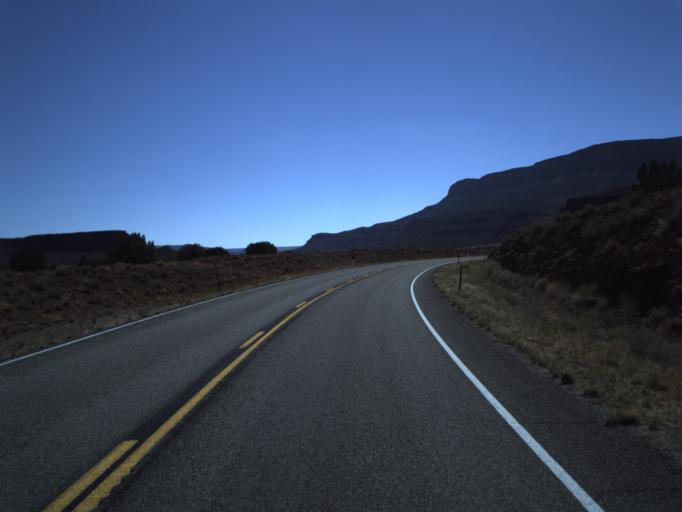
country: US
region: Utah
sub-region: San Juan County
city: Blanding
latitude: 37.7000
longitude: -110.2327
